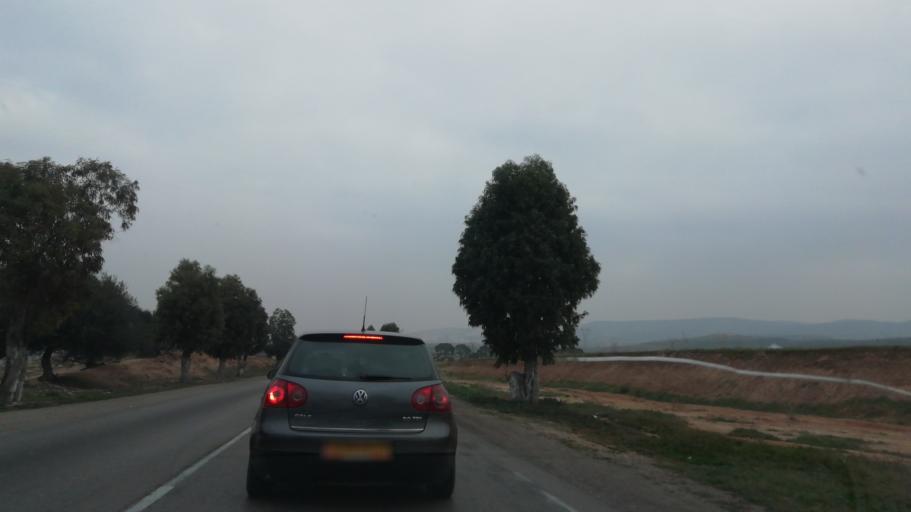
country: DZ
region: Mascara
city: Sig
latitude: 35.5389
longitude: -0.3432
